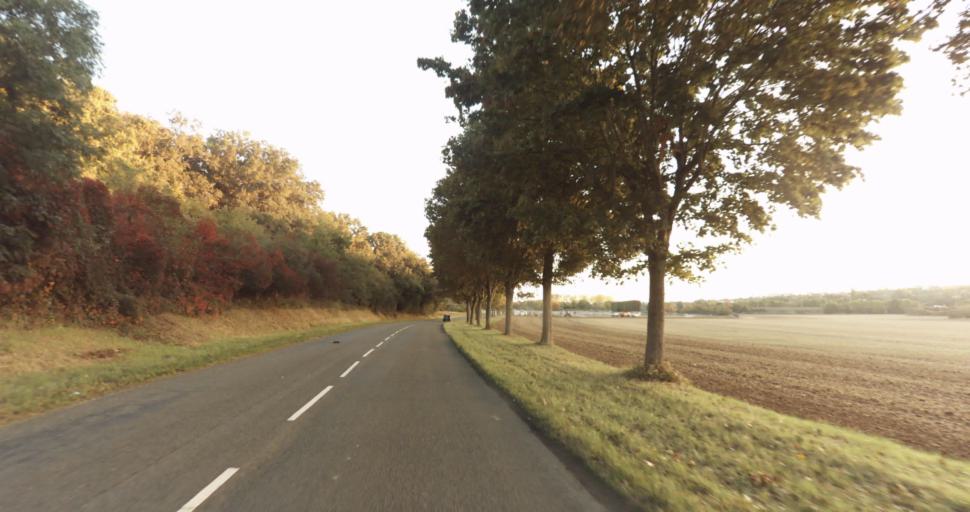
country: FR
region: Centre
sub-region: Departement d'Eure-et-Loir
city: Garnay
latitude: 48.7152
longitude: 1.3450
